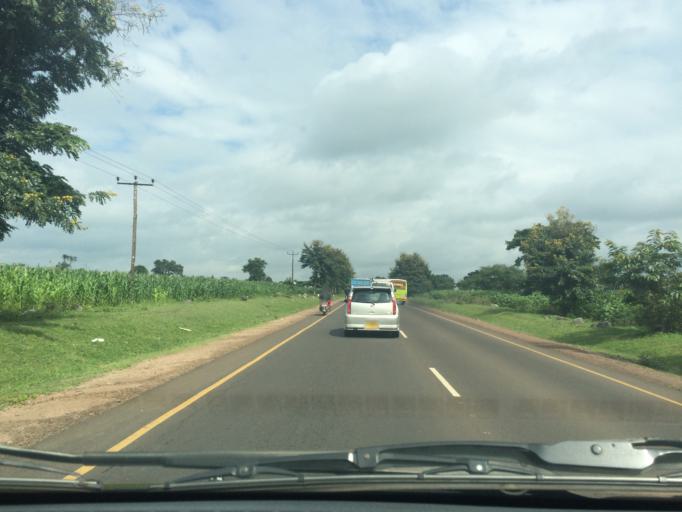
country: TZ
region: Arusha
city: Usa River
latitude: -3.3880
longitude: 36.9543
